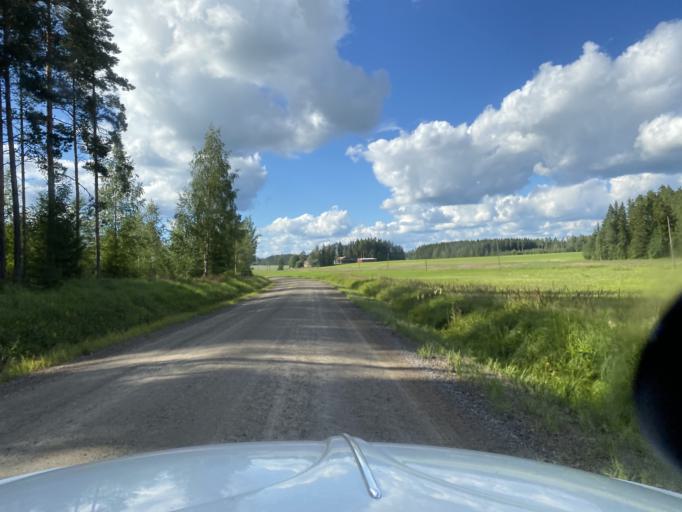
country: FI
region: Pirkanmaa
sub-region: Lounais-Pirkanmaa
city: Punkalaidun
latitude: 61.1253
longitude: 23.2583
